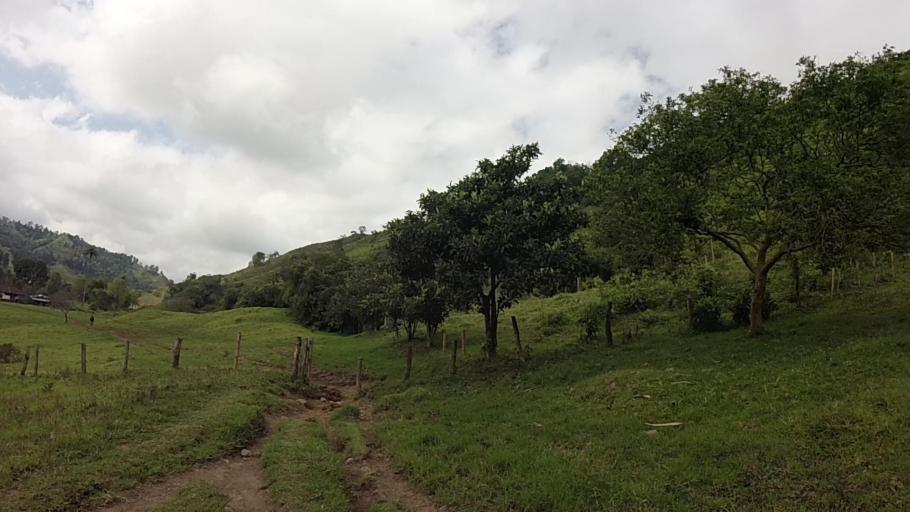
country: CO
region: Quindio
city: Salento
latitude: 4.6500
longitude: -75.5765
